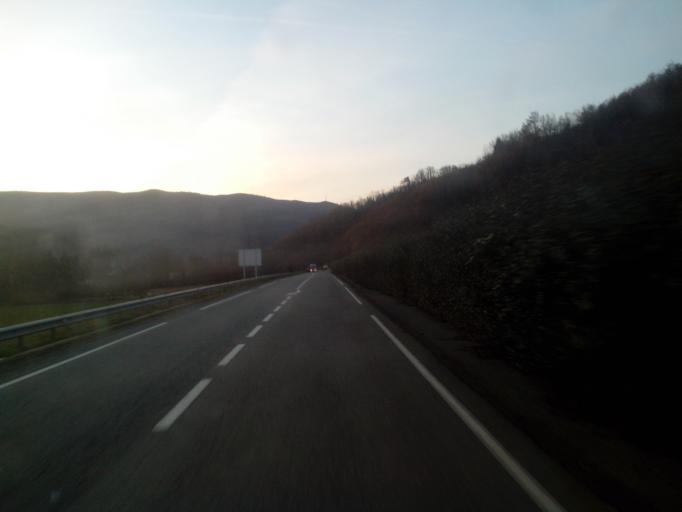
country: FR
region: Midi-Pyrenees
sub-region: Departement de l'Ariege
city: Saint-Paul-de-Jarrat
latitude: 42.9149
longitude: 1.6705
